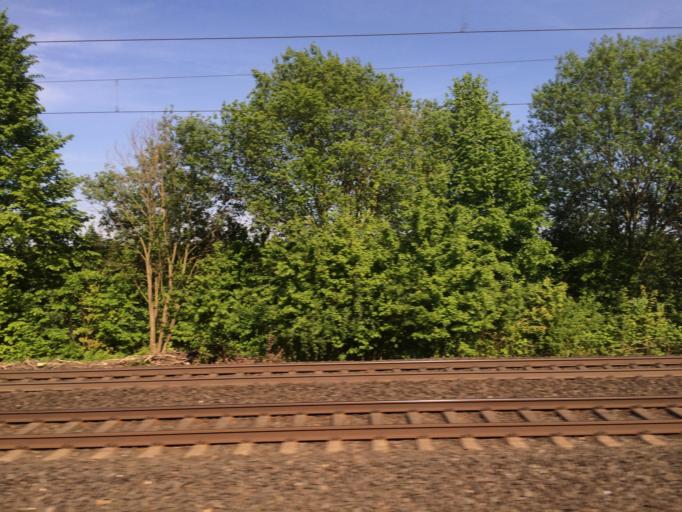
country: DE
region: North Rhine-Westphalia
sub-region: Regierungsbezirk Koln
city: Leverkusen
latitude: 51.0025
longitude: 6.9988
